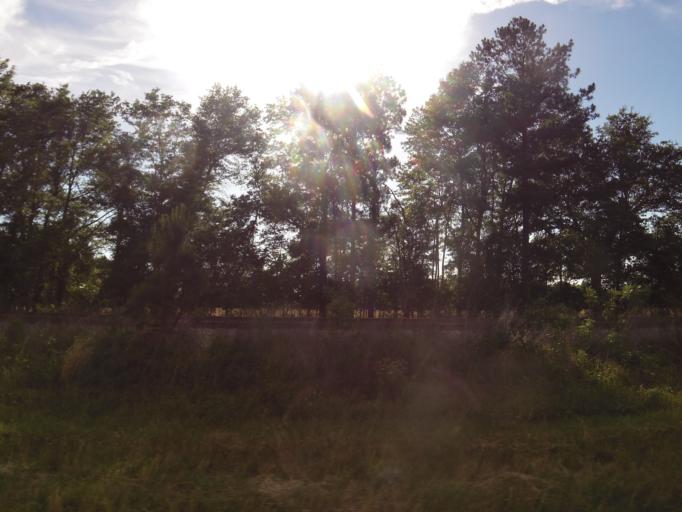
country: US
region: South Carolina
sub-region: Hampton County
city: Estill
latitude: 32.8444
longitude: -81.2392
